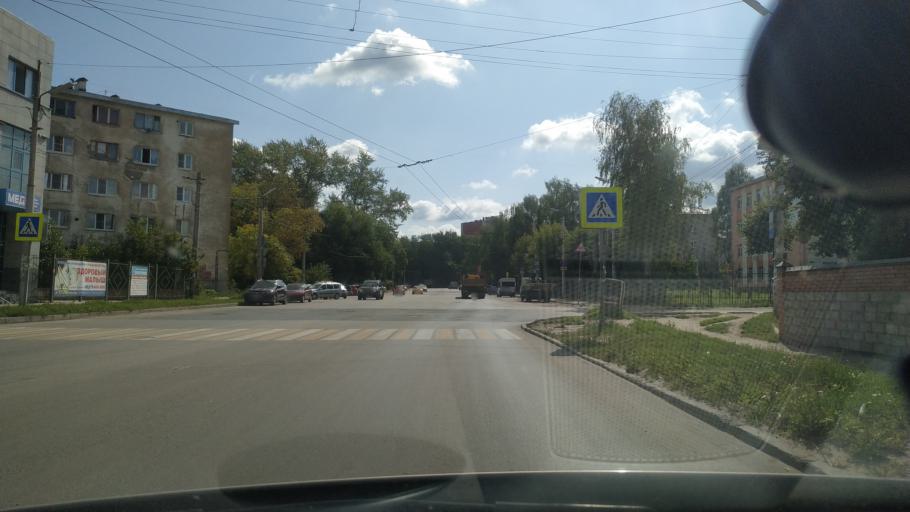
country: RU
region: Rjazan
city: Ryazan'
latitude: 54.6072
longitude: 39.7029
